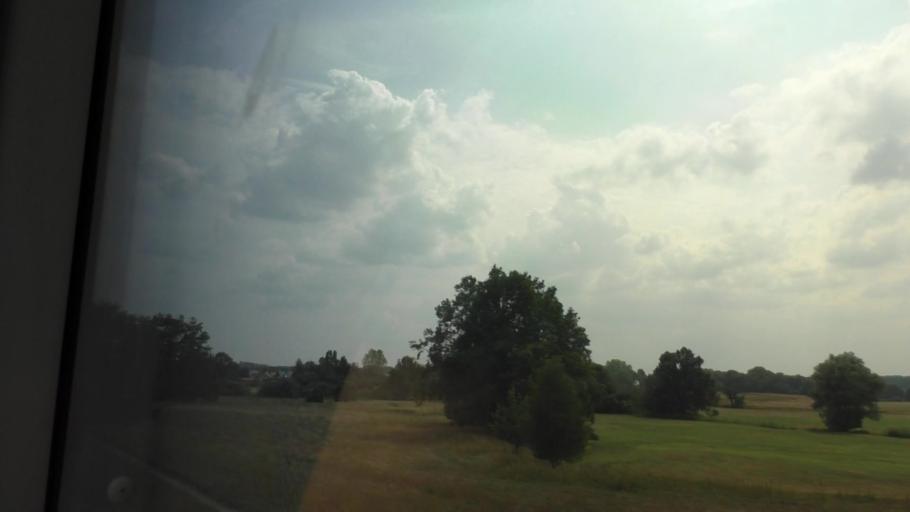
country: DE
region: Brandenburg
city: Beeskow
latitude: 52.1763
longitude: 14.2634
